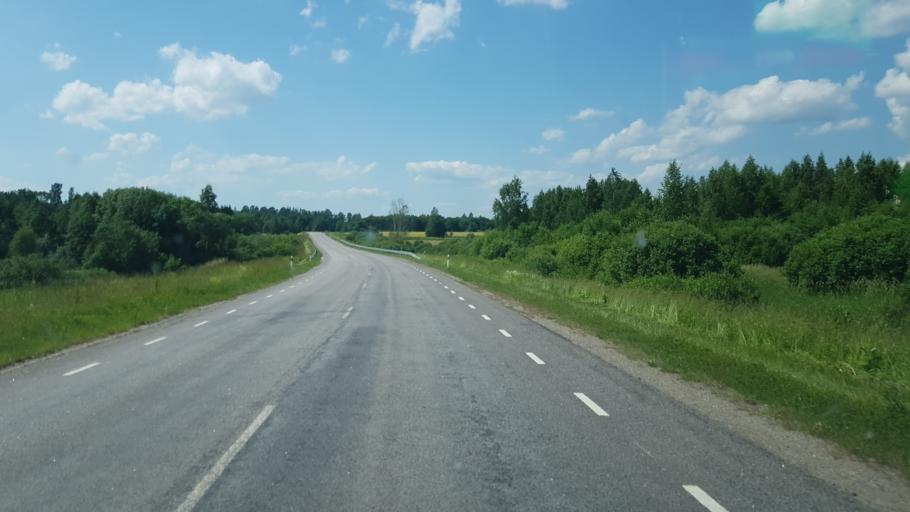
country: EE
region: Tartu
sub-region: Alatskivi vald
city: Kallaste
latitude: 58.5269
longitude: 27.0586
